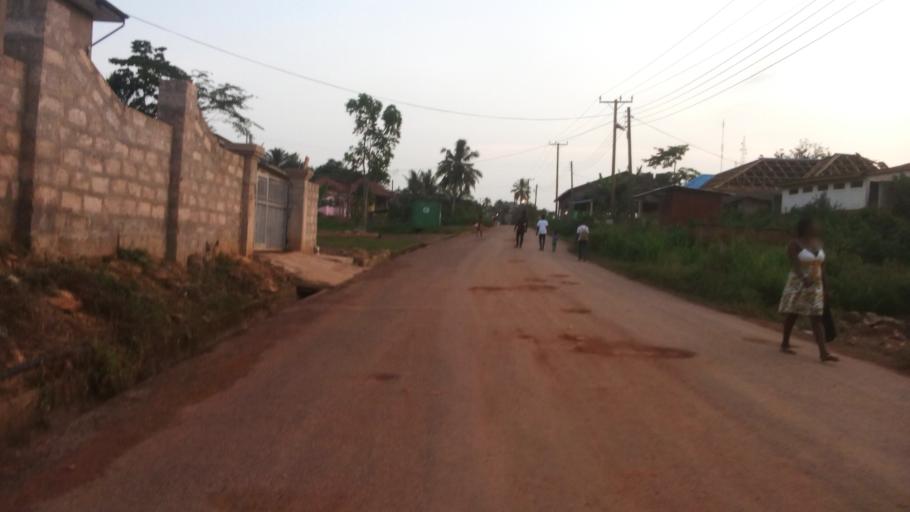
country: GH
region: Western
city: Tarkwa
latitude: 5.3088
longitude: -1.9995
